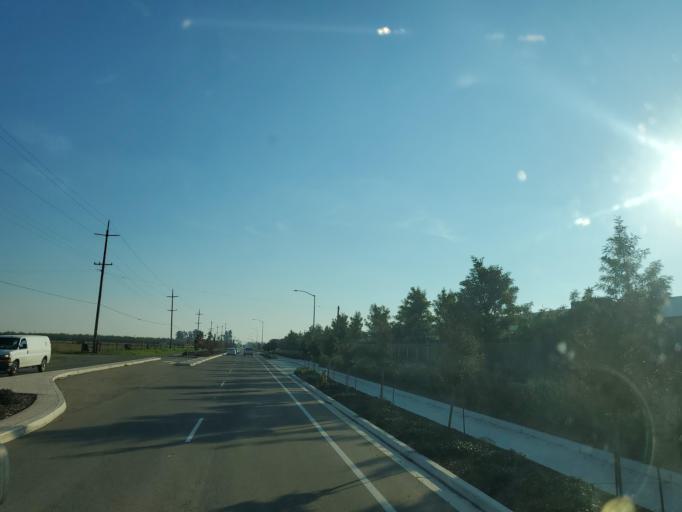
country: US
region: California
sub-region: San Joaquin County
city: French Camp
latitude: 37.8535
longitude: -121.2555
